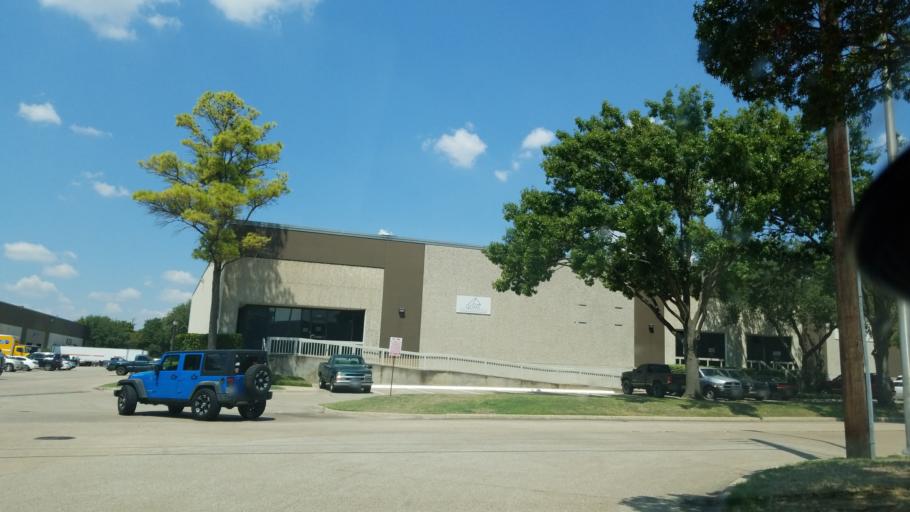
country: US
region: Texas
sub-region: Dallas County
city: Richardson
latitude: 32.8928
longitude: -96.7076
